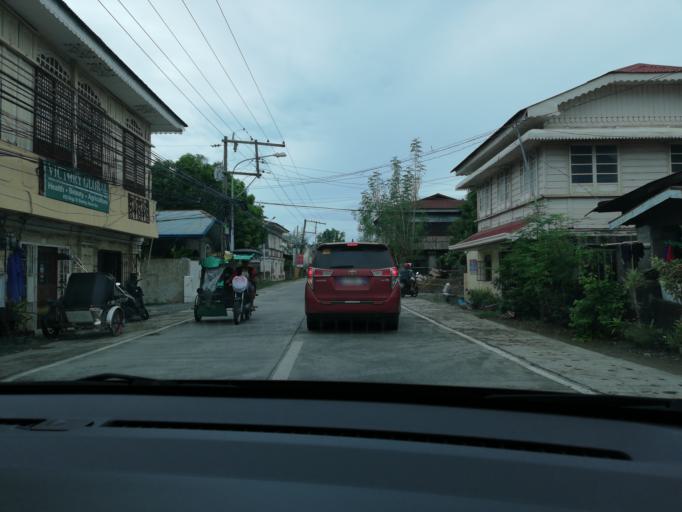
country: PH
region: Ilocos
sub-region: Province of Ilocos Sur
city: Bantay
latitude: 17.5826
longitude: 120.3862
